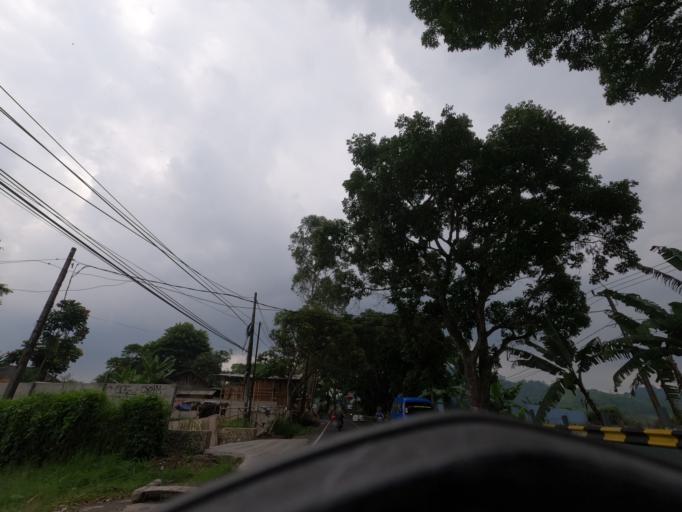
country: ID
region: West Java
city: Sukabumi
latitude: -6.7735
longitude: 107.0634
